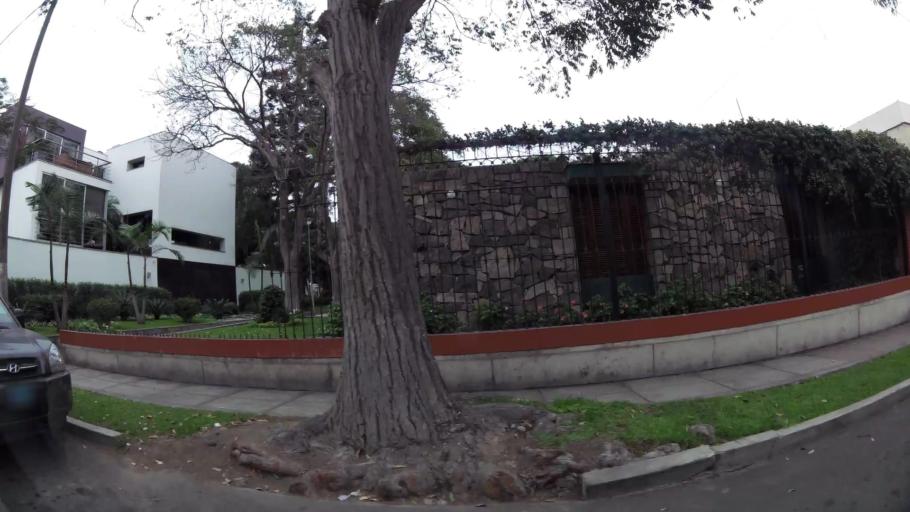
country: PE
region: Lima
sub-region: Lima
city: Surco
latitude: -12.1197
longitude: -77.0138
